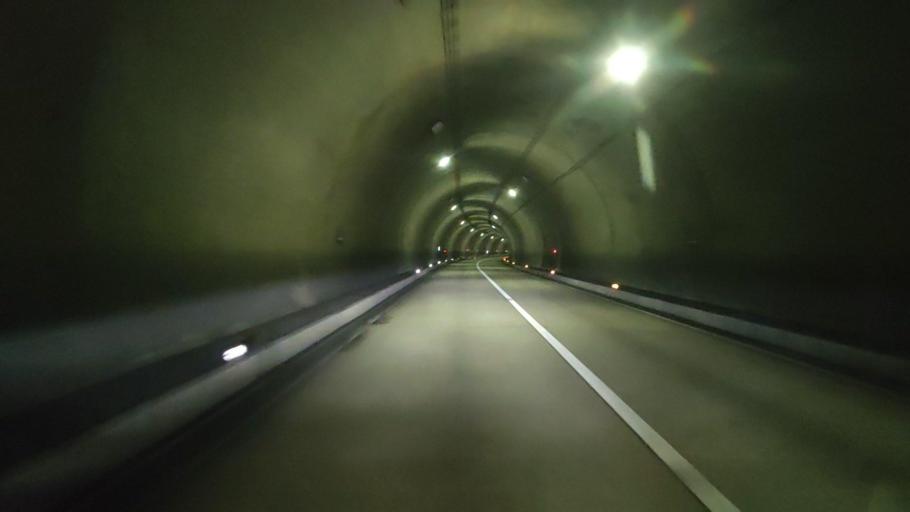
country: JP
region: Wakayama
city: Shingu
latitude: 33.8514
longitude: 135.8564
